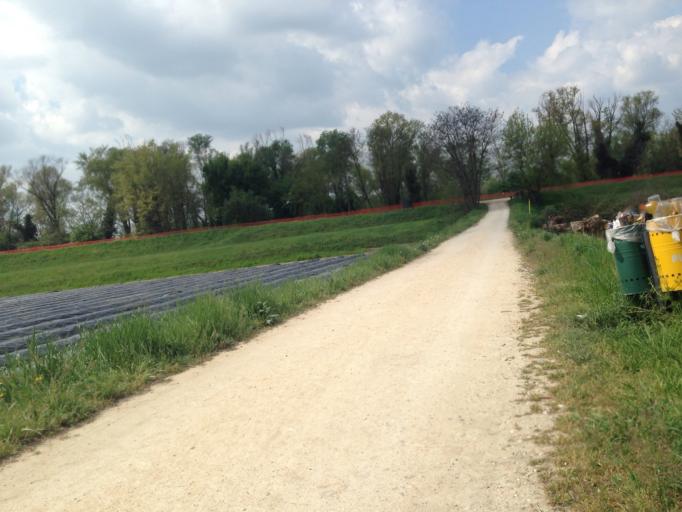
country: IT
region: Veneto
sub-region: Provincia di Verona
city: Campagnola
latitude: 45.3798
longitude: 11.0737
